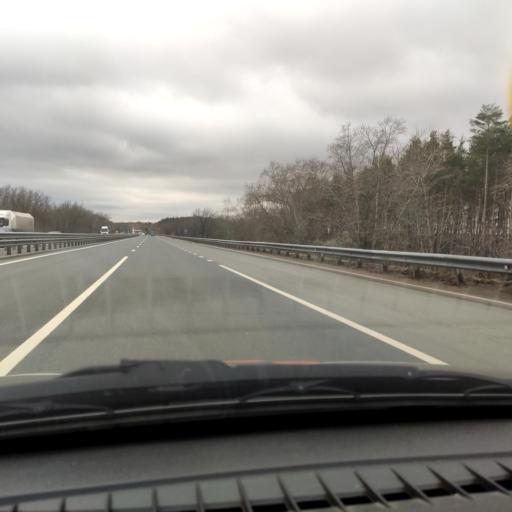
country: RU
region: Samara
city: Zhigulevsk
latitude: 53.5142
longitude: 49.5893
